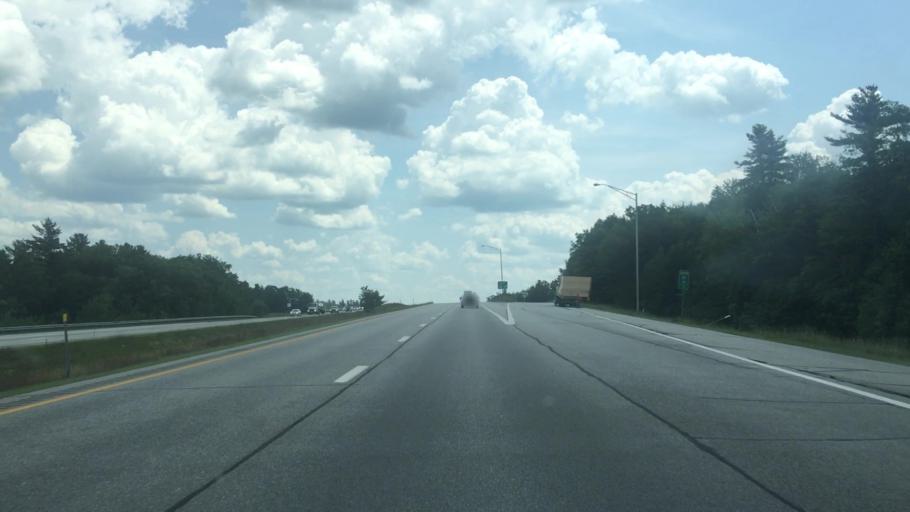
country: US
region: New Hampshire
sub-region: Merrimack County
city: New London
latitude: 43.4265
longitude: -72.0396
